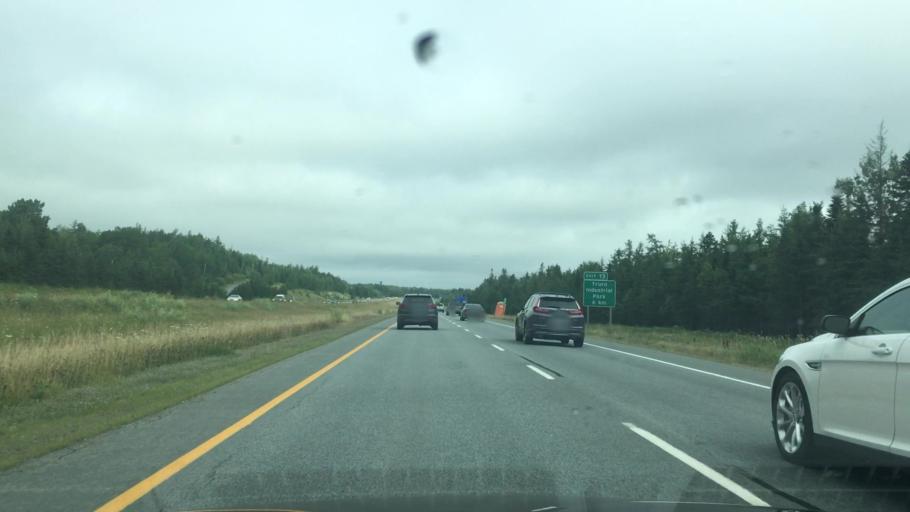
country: CA
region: Nova Scotia
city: Truro
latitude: 45.2920
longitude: -63.3004
